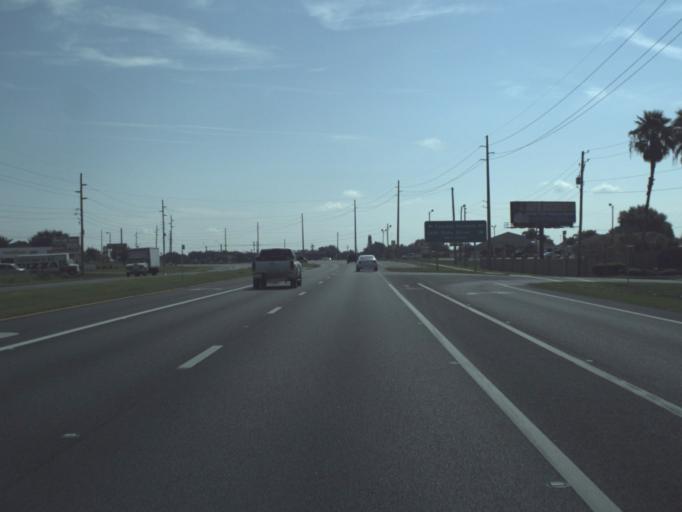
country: US
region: Florida
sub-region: Polk County
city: Cypress Gardens
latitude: 27.9791
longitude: -81.6666
